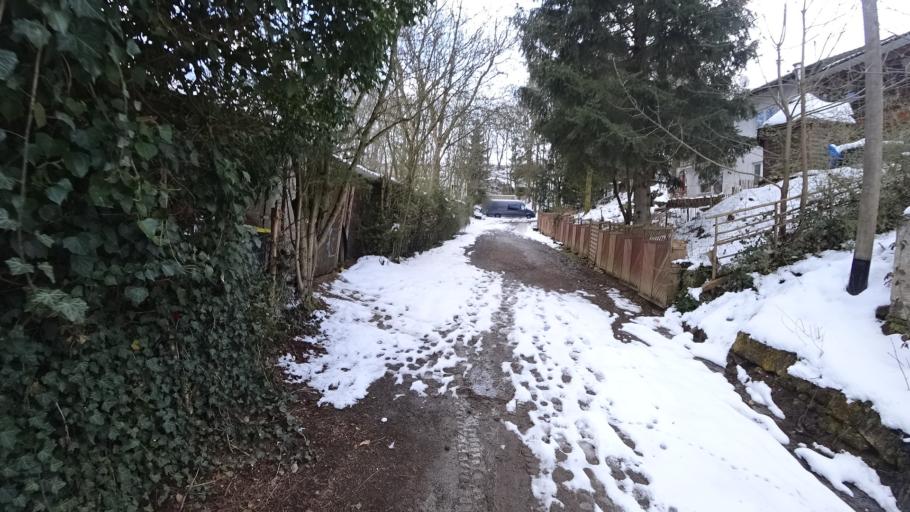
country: DE
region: Rheinland-Pfalz
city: Elkenroth
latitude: 50.7312
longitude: 7.8805
